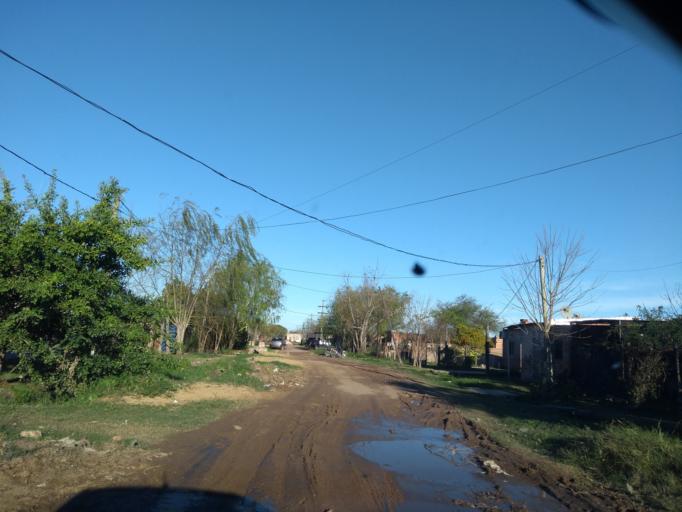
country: AR
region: Chaco
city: Barranqueras
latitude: -27.4923
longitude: -58.9378
